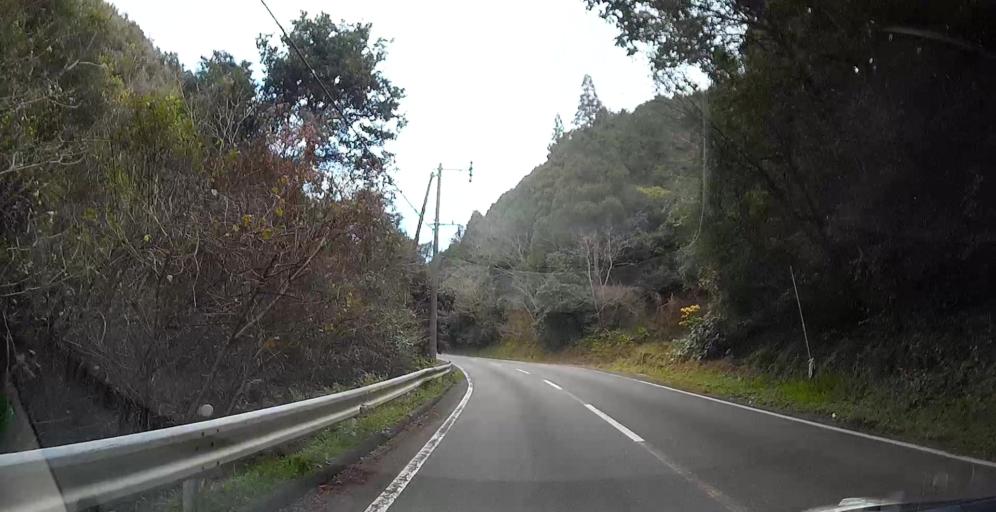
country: JP
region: Kumamoto
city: Yatsushiro
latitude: 32.3705
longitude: 130.5047
